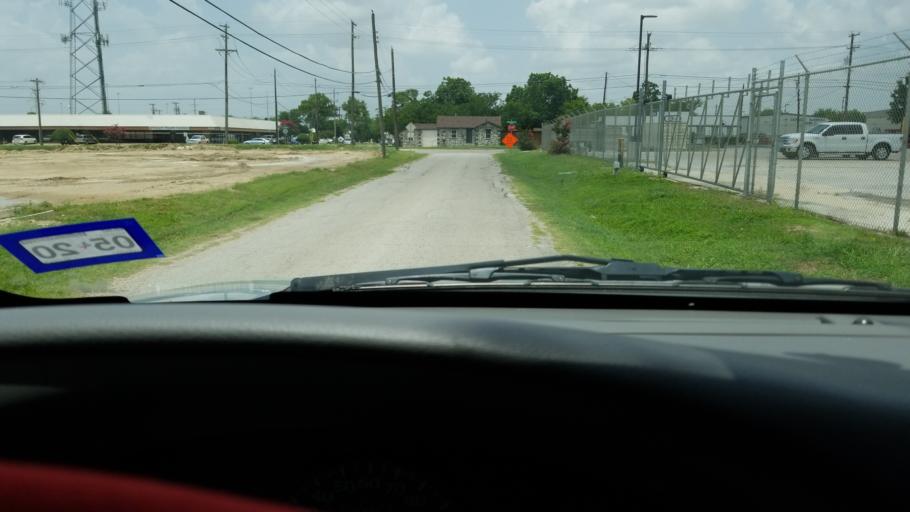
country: US
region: Texas
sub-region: Dallas County
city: Irving
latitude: 32.8299
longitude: -96.9114
